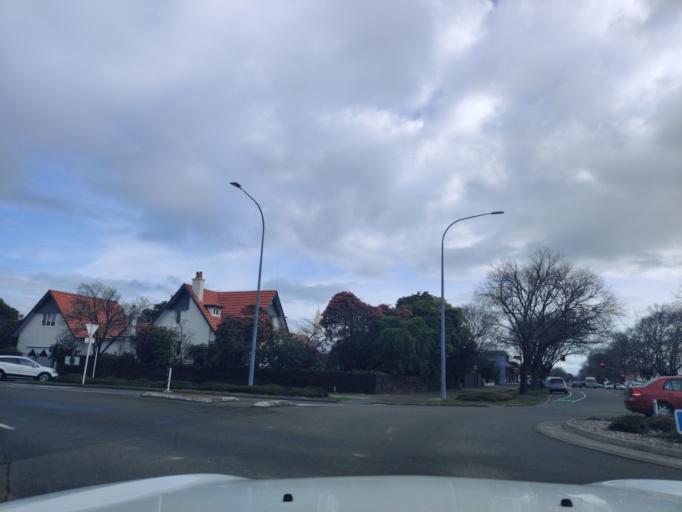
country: NZ
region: Manawatu-Wanganui
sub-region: Palmerston North City
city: Palmerston North
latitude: -40.3535
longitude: 175.6207
